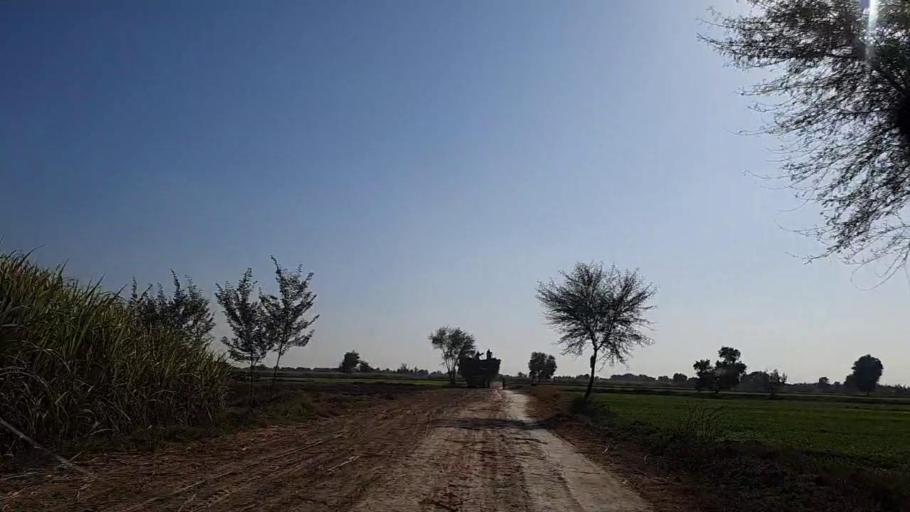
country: PK
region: Sindh
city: Khanpur
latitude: 27.7770
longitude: 69.3660
